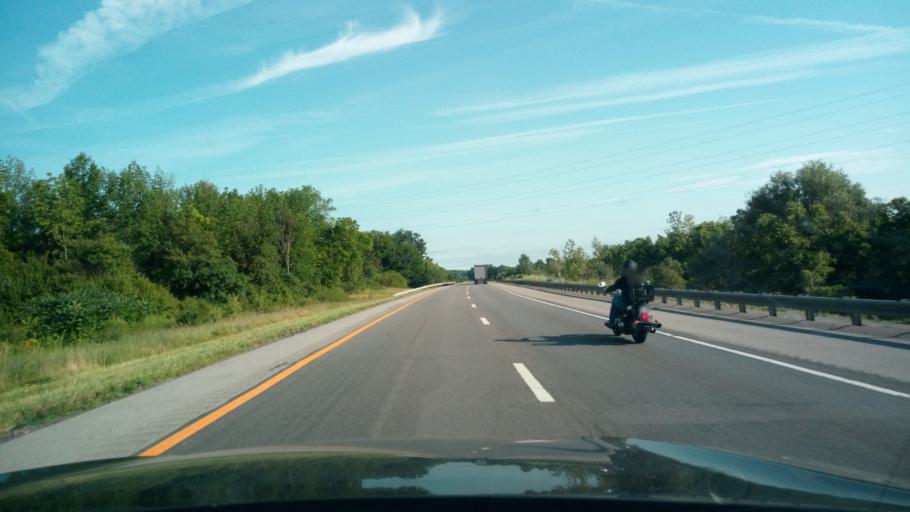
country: US
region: New York
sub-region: Livingston County
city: Dansville
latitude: 42.5875
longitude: -77.7470
